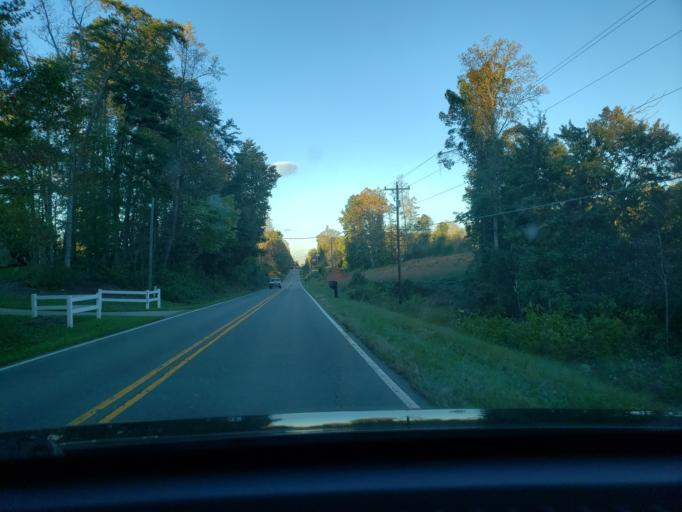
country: US
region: North Carolina
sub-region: Stokes County
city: Danbury
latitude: 36.3560
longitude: -80.2144
